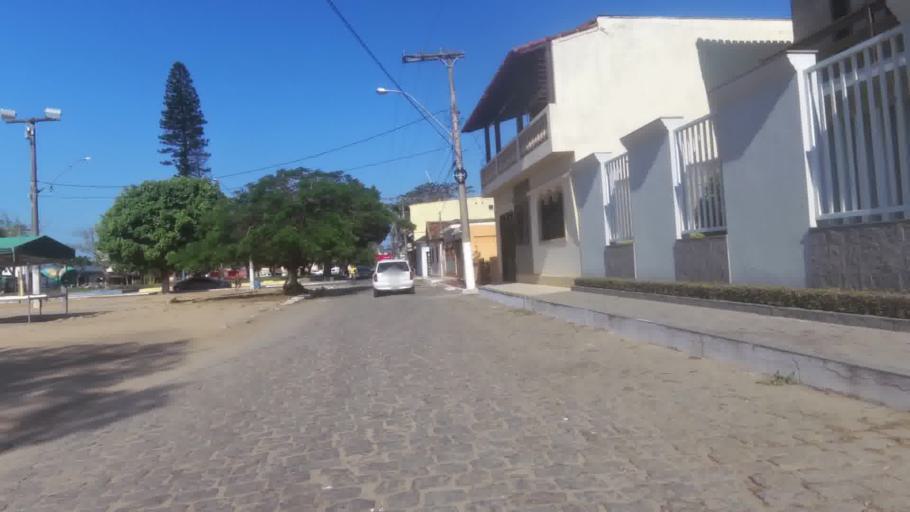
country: BR
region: Espirito Santo
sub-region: Itapemirim
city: Itapemirim
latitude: -21.0095
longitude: -40.8107
